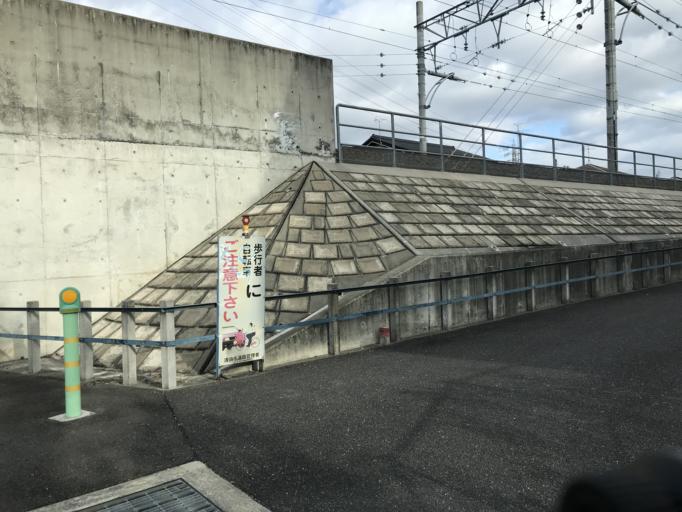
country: JP
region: Aichi
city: Nagoya-shi
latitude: 35.1974
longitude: 136.8389
